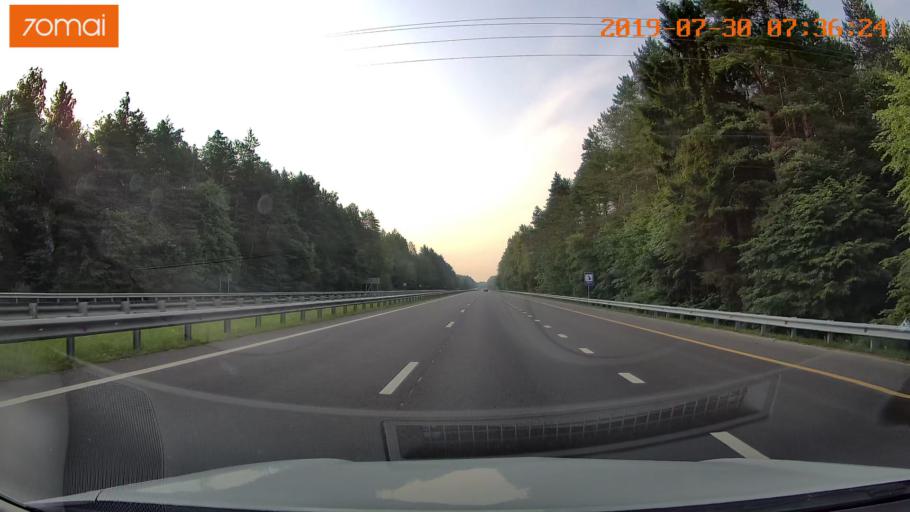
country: RU
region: Kaliningrad
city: Gvardeysk
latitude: 54.6649
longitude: 21.1235
